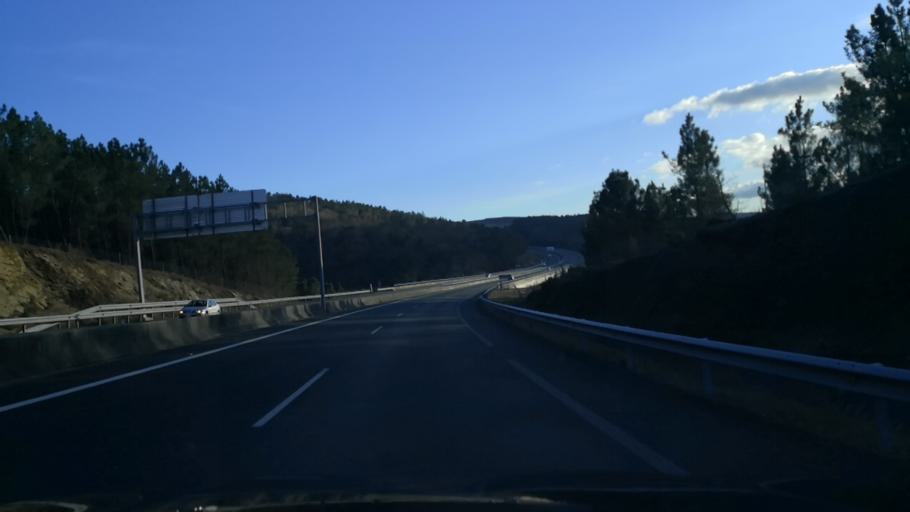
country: ES
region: Galicia
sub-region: Provincia de Pontevedra
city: Lalin
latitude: 42.6167
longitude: -8.0983
